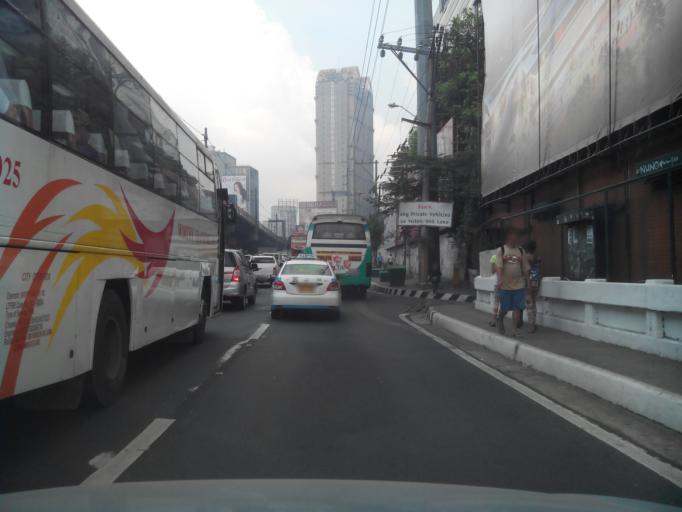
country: PH
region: Metro Manila
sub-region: Mandaluyong
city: Mandaluyong City
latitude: 14.5690
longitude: 121.0463
